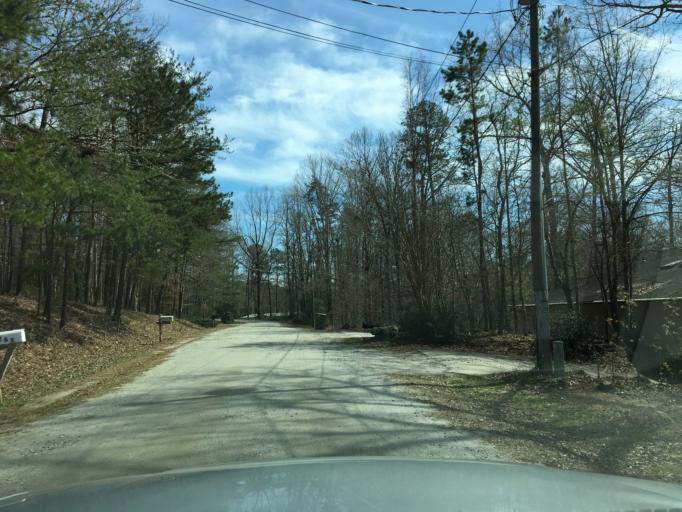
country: US
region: South Carolina
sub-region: Spartanburg County
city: Duncan
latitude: 34.9188
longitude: -82.1237
